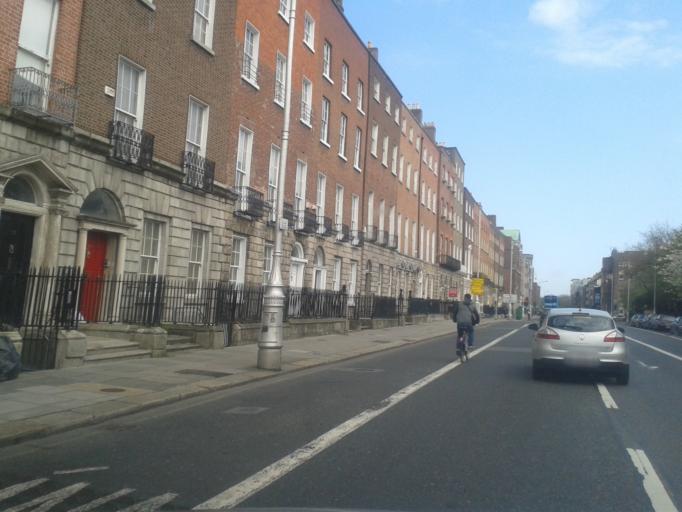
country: IE
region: Leinster
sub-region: Dublin City
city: Dublin
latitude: 53.3404
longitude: -6.2487
